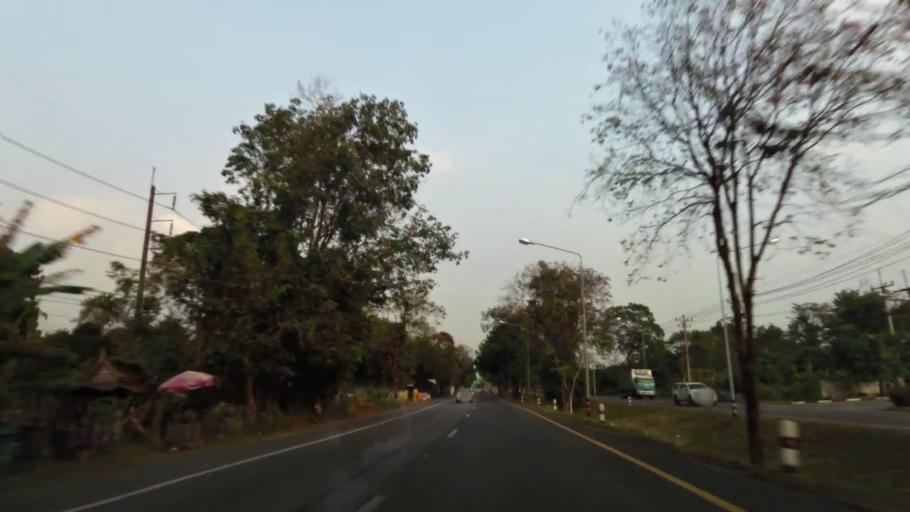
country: TH
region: Chanthaburi
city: Khlung
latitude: 12.4653
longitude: 102.2134
